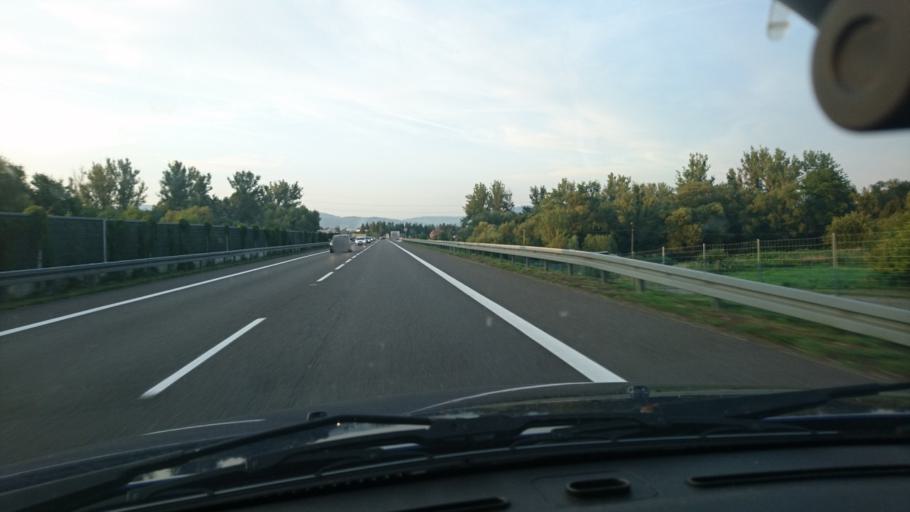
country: PL
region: Silesian Voivodeship
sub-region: Powiat zywiecki
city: Wieprz
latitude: 49.6651
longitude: 19.1680
